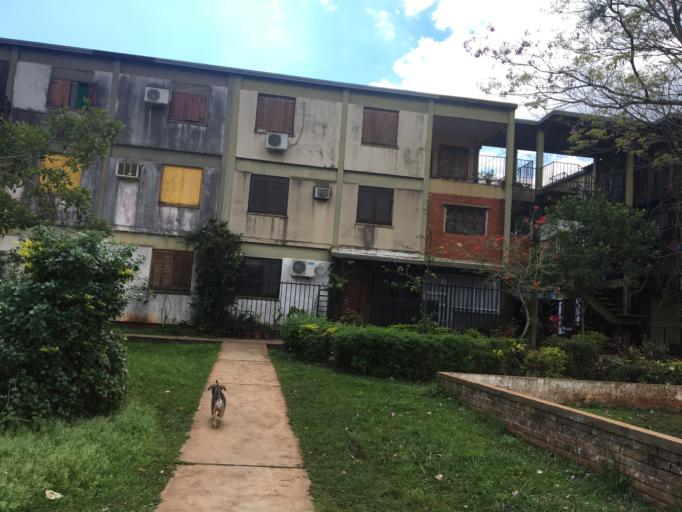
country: AR
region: Misiones
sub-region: Departamento de Capital
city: Posadas
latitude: -27.3947
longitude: -55.9062
